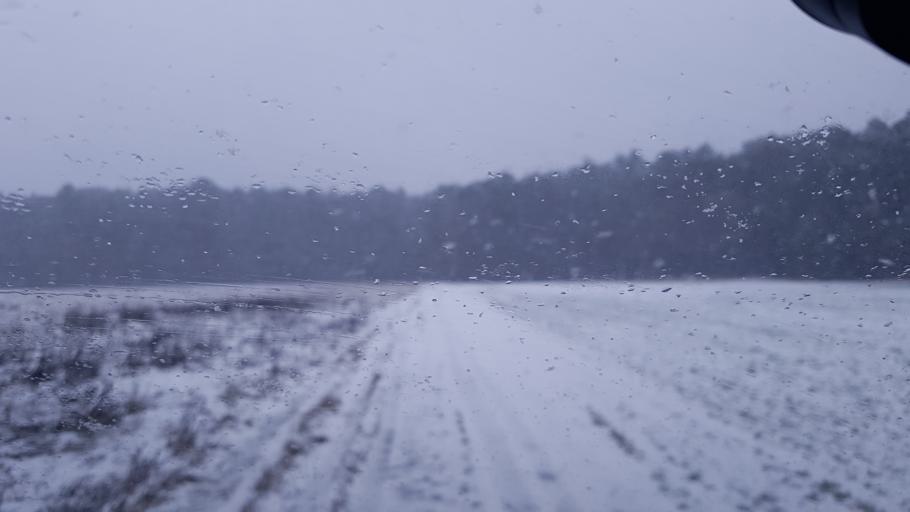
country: DE
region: Brandenburg
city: Schenkendobern
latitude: 51.9013
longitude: 14.5954
